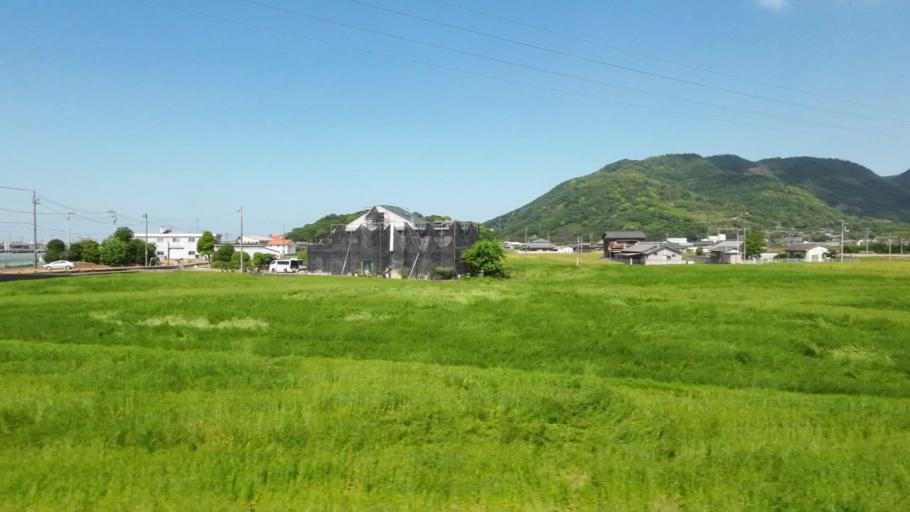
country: JP
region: Kagawa
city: Kan'onjicho
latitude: 34.1362
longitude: 133.6844
